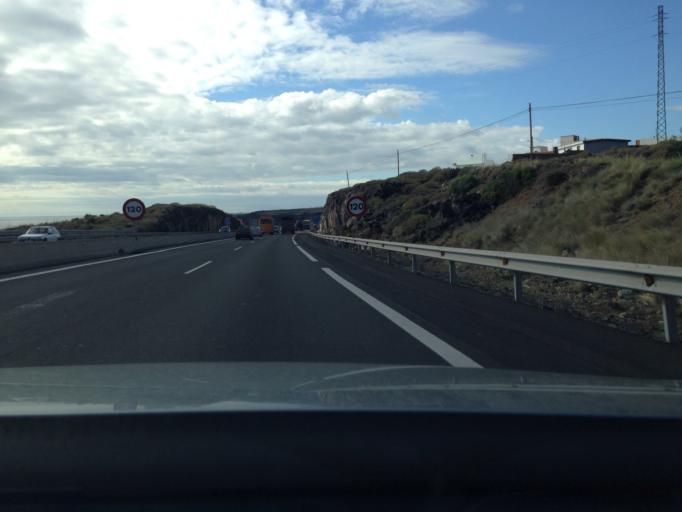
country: ES
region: Canary Islands
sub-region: Provincia de Santa Cruz de Tenerife
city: Fasnia
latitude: 28.1969
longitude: -16.4265
